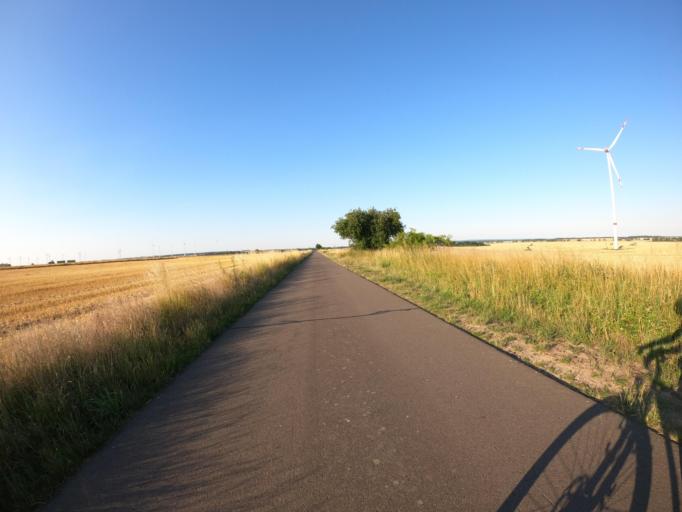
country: DE
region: Brandenburg
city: Tantow
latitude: 53.2901
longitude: 14.3732
